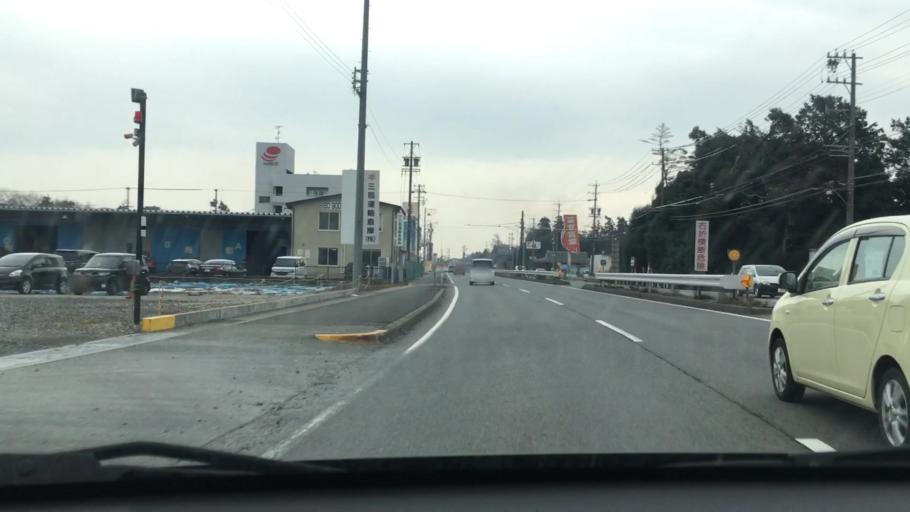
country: JP
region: Mie
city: Suzuka
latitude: 34.9145
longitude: 136.5705
